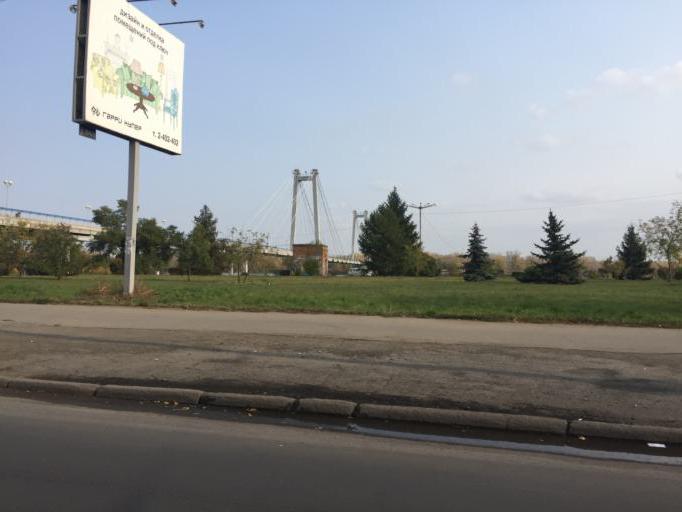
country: RU
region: Krasnoyarskiy
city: Krasnoyarsk
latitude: 56.0131
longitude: 92.8967
